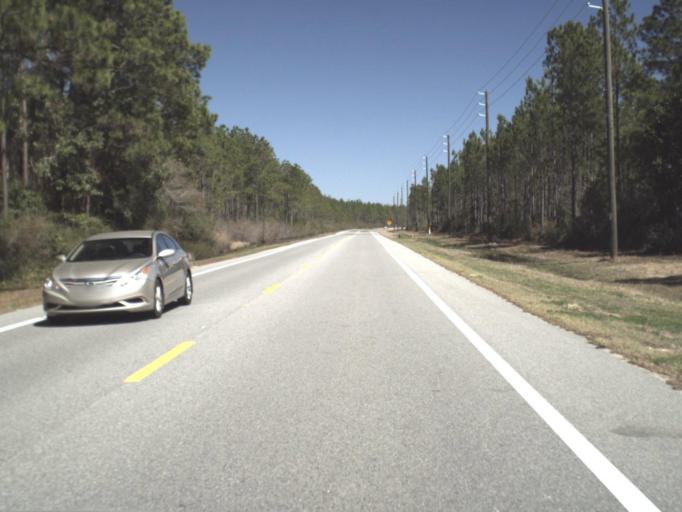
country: US
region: Florida
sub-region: Bay County
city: Panama City Beach
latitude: 30.3173
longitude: -85.8063
